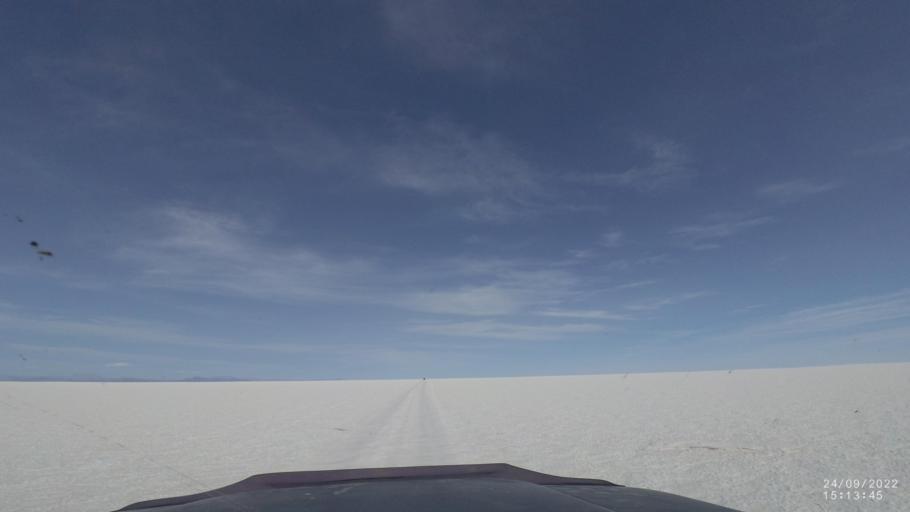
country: BO
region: Potosi
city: Colchani
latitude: -19.9582
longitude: -67.4622
